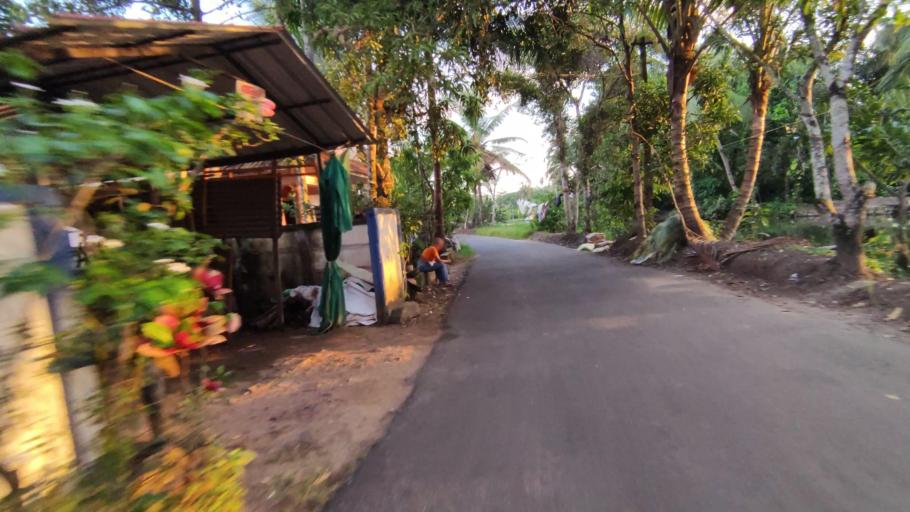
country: IN
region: Kerala
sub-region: Kottayam
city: Kottayam
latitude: 9.5775
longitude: 76.4465
